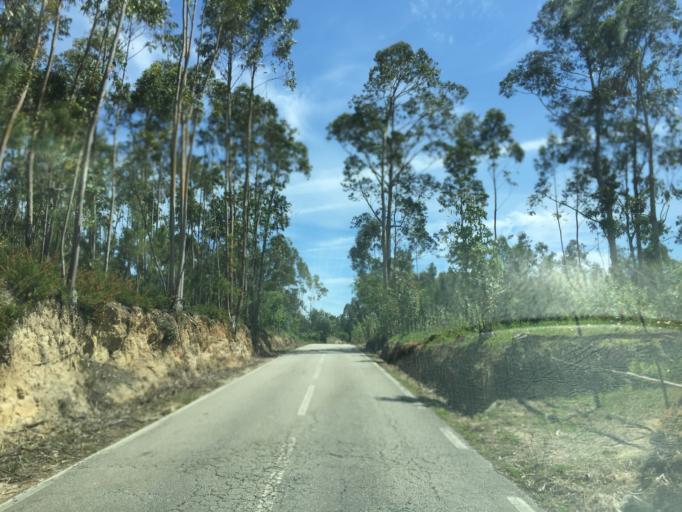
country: PT
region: Leiria
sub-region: Pombal
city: Lourical
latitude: 40.0659
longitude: -8.7220
